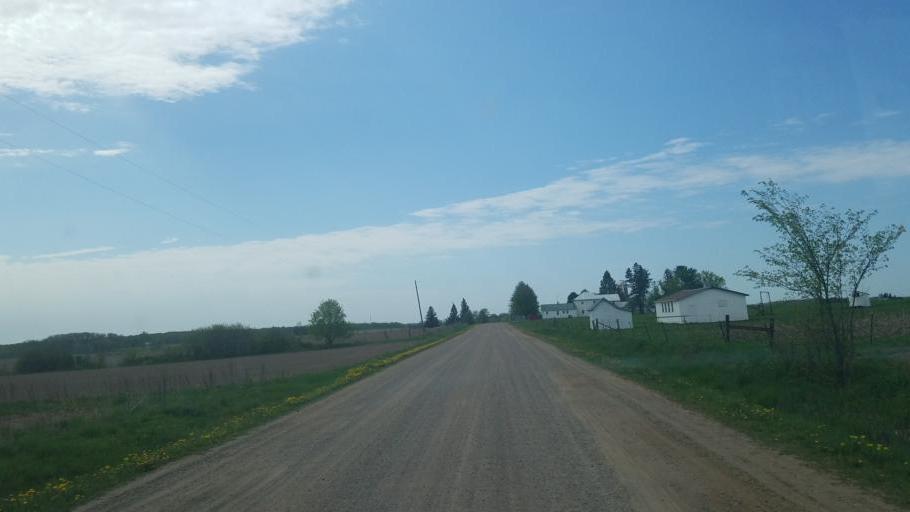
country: US
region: Wisconsin
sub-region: Marathon County
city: Spencer
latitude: 44.6382
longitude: -90.3770
